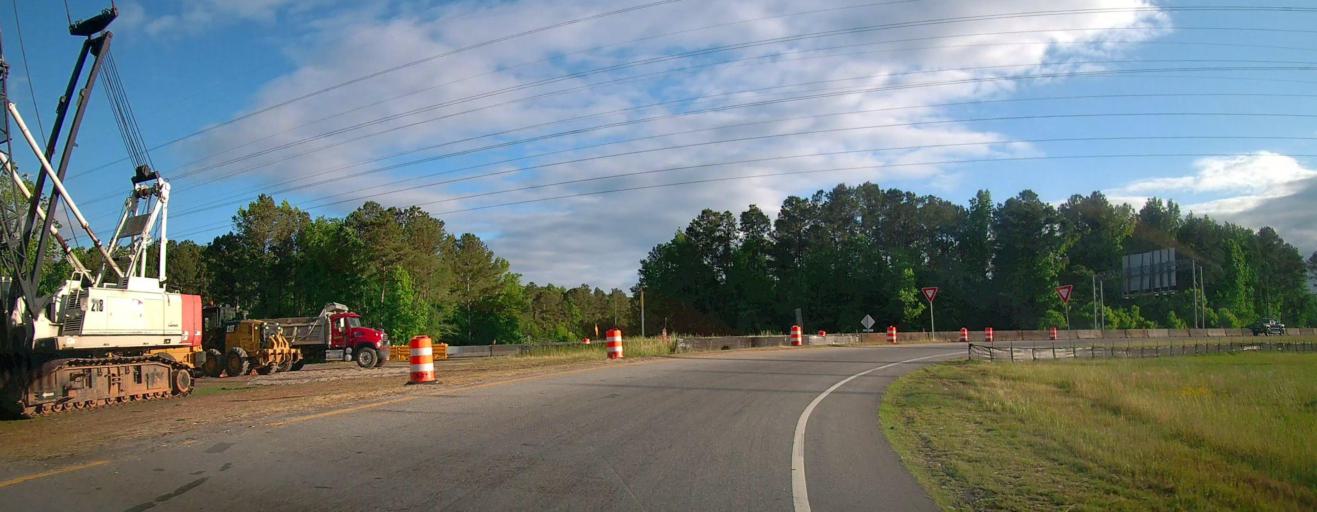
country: US
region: Georgia
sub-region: Clarke County
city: Athens
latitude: 33.9788
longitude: -83.3504
